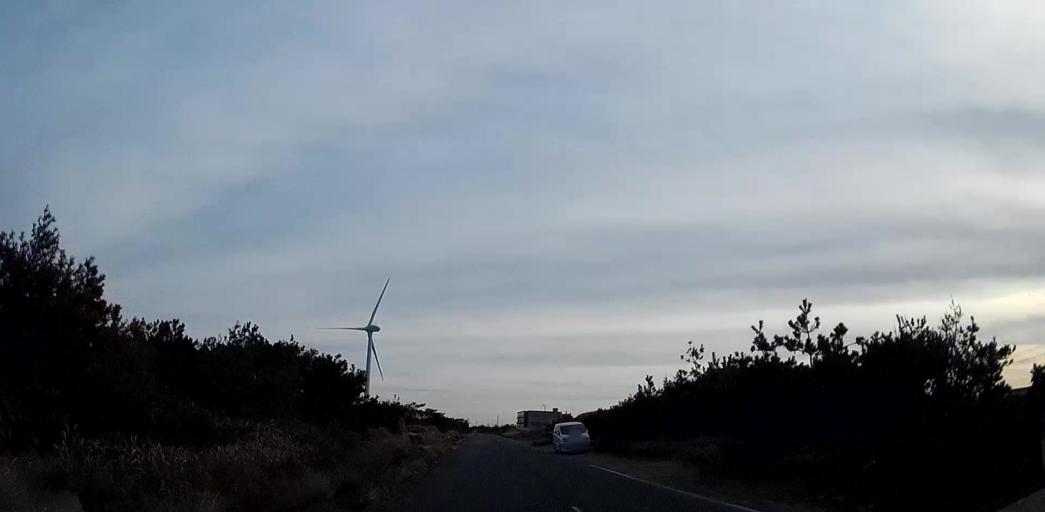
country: JP
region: Chiba
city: Hasaki
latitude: 35.7953
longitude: 140.7942
